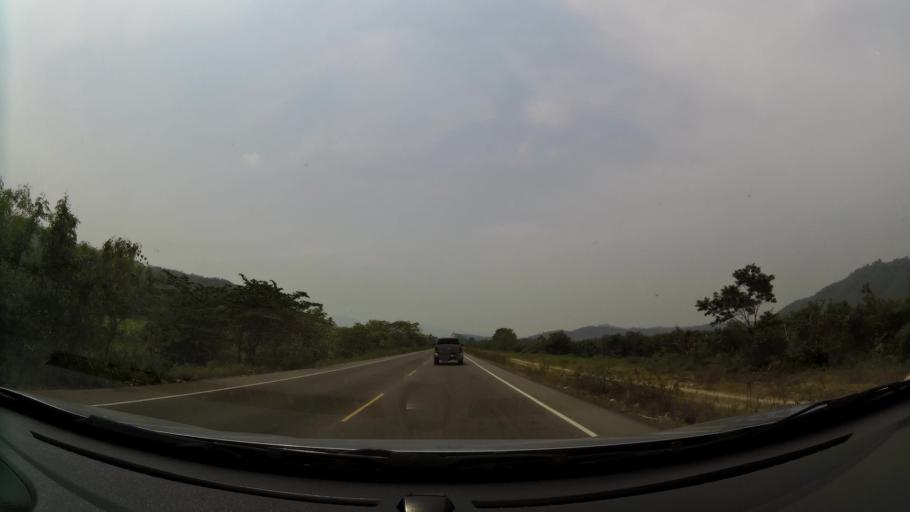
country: HN
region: Cortes
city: Potrerillos
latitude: 15.2545
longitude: -87.9571
